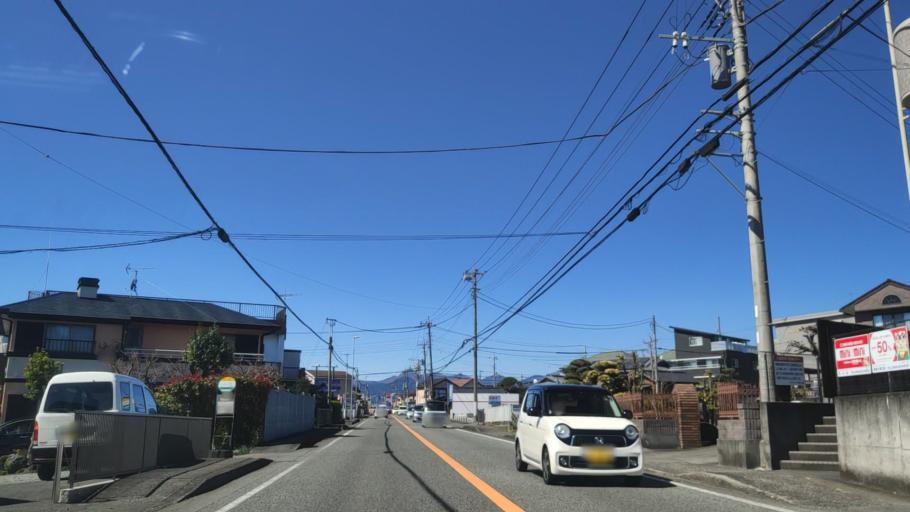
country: JP
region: Shizuoka
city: Fujinomiya
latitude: 35.2080
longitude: 138.6387
